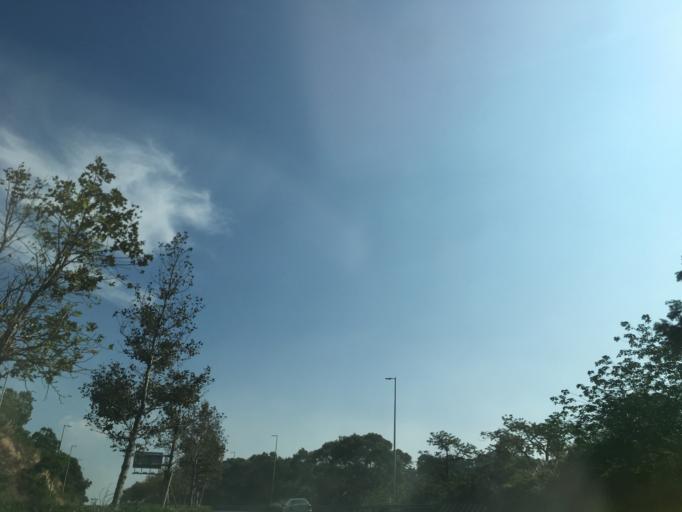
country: TW
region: Taiwan
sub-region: Hsinchu
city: Hsinchu
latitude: 24.7698
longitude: 120.9523
